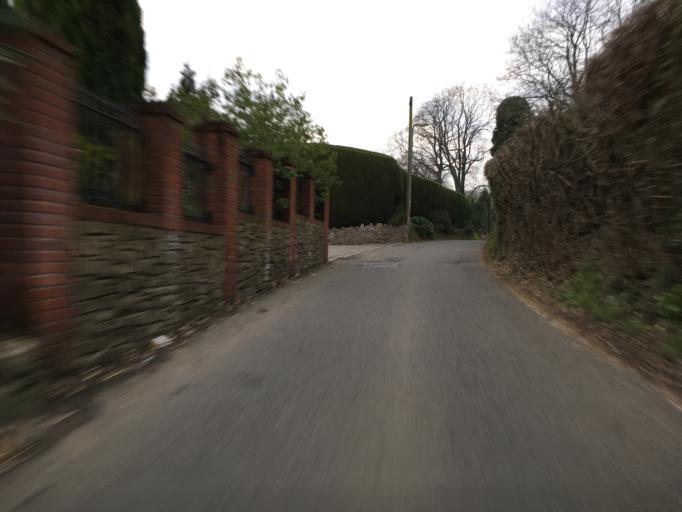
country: GB
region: Wales
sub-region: Newport
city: Marshfield
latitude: 51.5745
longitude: -3.0603
